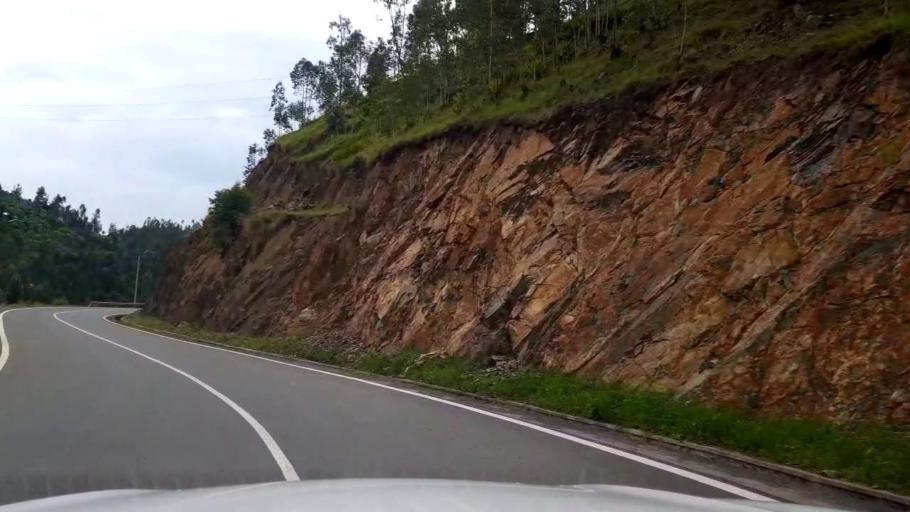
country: RW
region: Western Province
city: Kibuye
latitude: -2.0303
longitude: 29.3984
